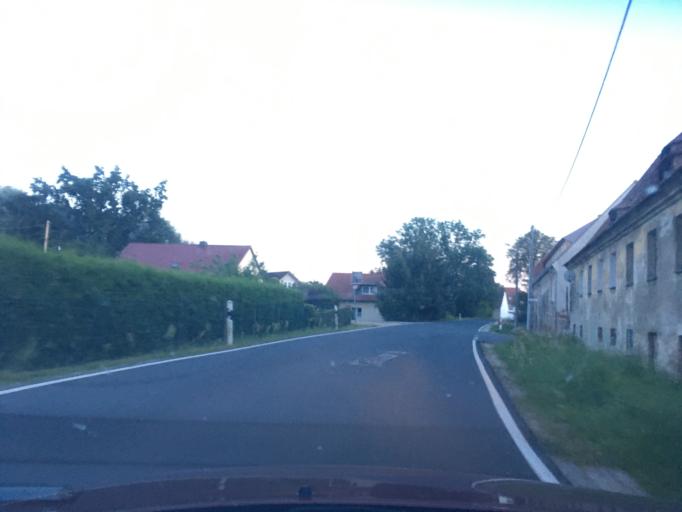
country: PL
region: Lower Silesian Voivodeship
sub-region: Powiat zgorzelecki
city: Piensk
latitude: 51.2192
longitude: 15.0046
